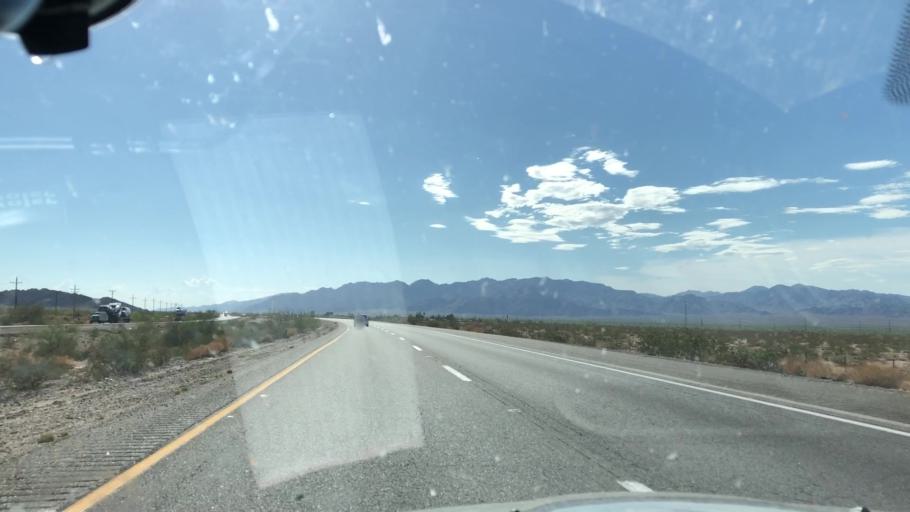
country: US
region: California
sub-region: Imperial County
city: Niland
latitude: 33.7105
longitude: -115.3767
